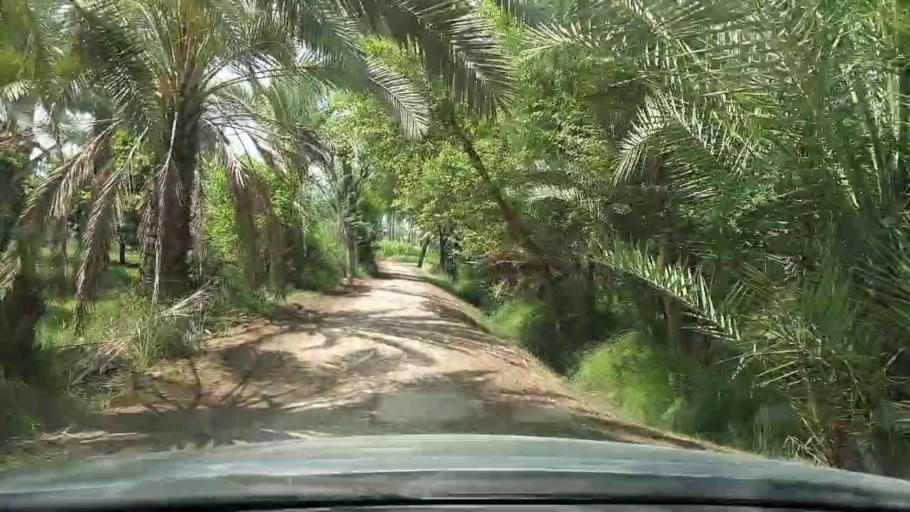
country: PK
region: Sindh
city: Kot Diji
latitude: 27.3964
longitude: 68.7497
